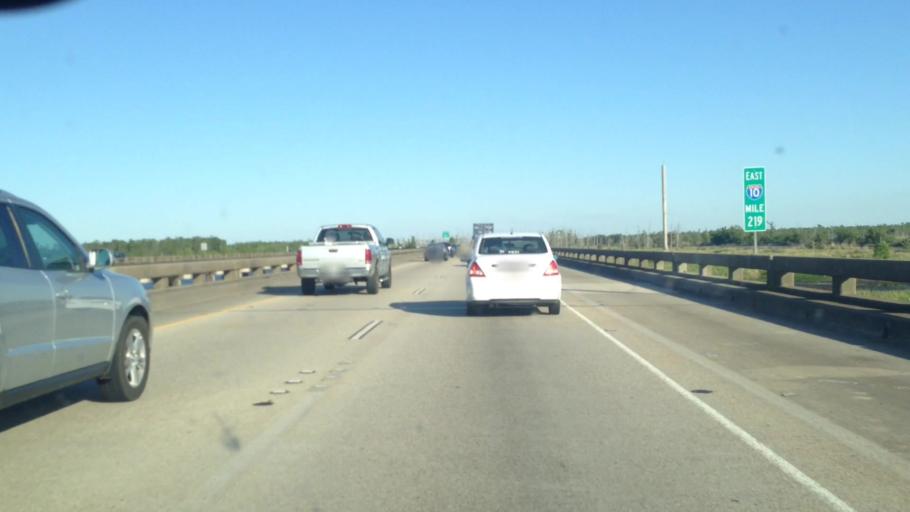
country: US
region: Louisiana
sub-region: Saint Charles Parish
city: Ama
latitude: 30.0137
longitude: -90.3105
